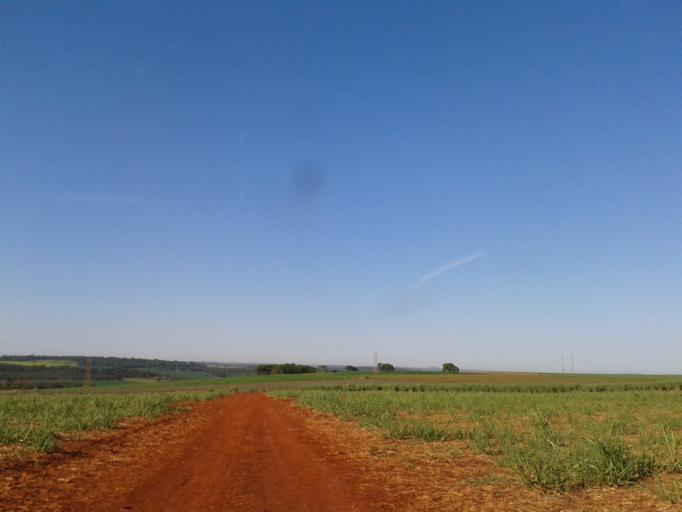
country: BR
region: Minas Gerais
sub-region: Centralina
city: Centralina
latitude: -18.6716
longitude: -49.2702
